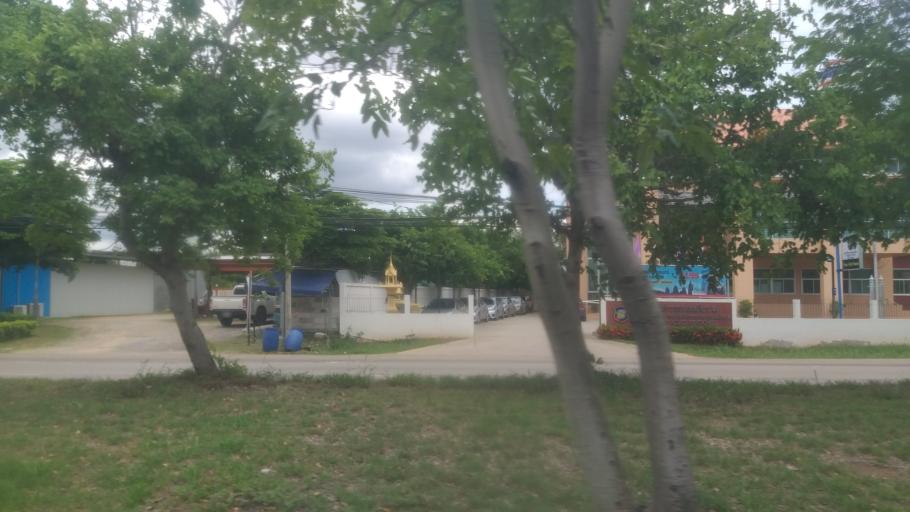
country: TH
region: Nakhon Ratchasima
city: Nakhon Ratchasima
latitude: 15.0395
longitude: 102.1357
